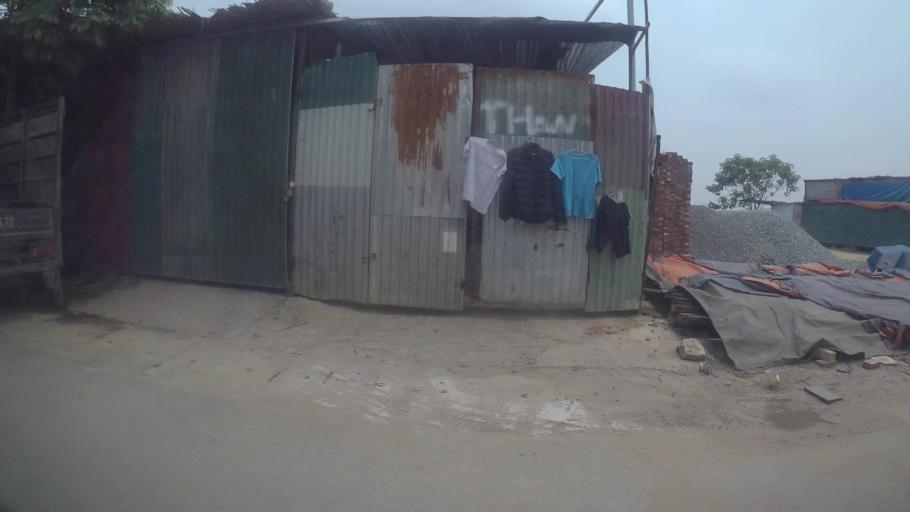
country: VN
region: Ha Noi
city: Ha Dong
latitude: 20.9928
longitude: 105.7406
